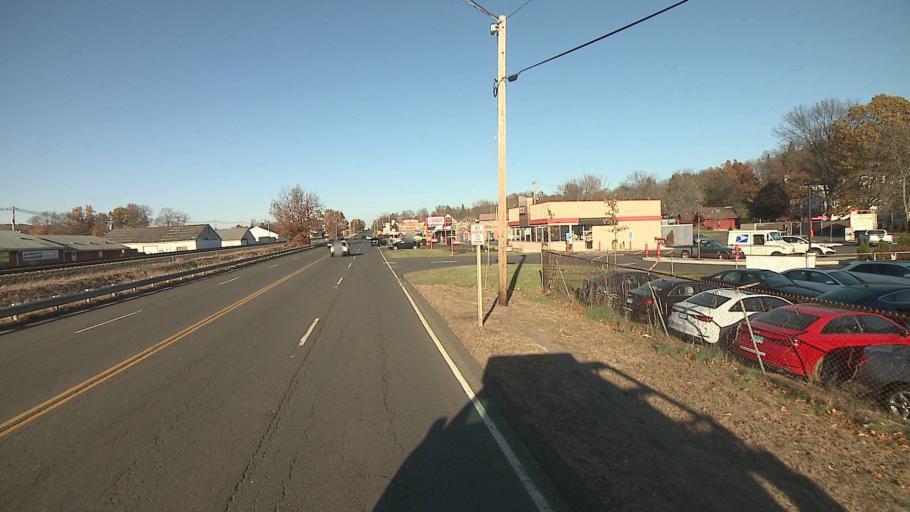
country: US
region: Connecticut
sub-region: New Haven County
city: Wallingford Center
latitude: 41.4406
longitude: -72.8319
